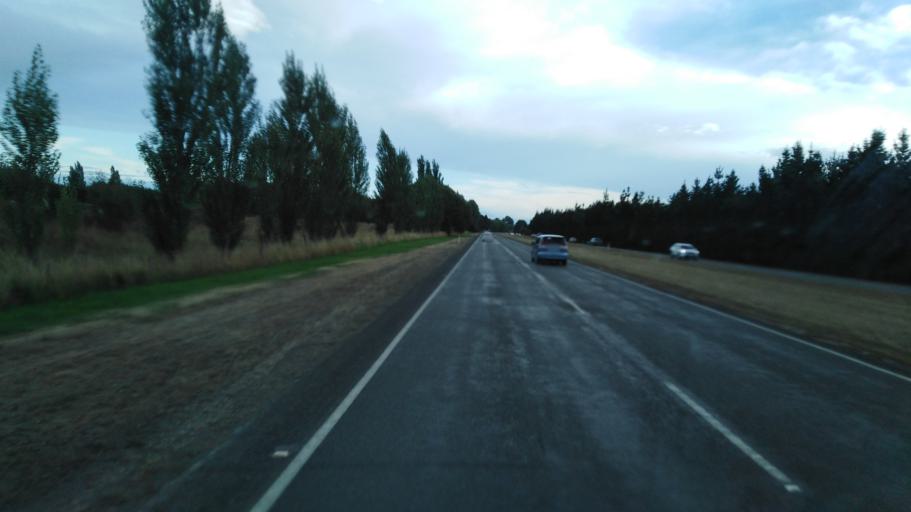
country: NZ
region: Canterbury
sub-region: Waimakariri District
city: Kaiapoi
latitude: -43.4005
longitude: 172.6422
